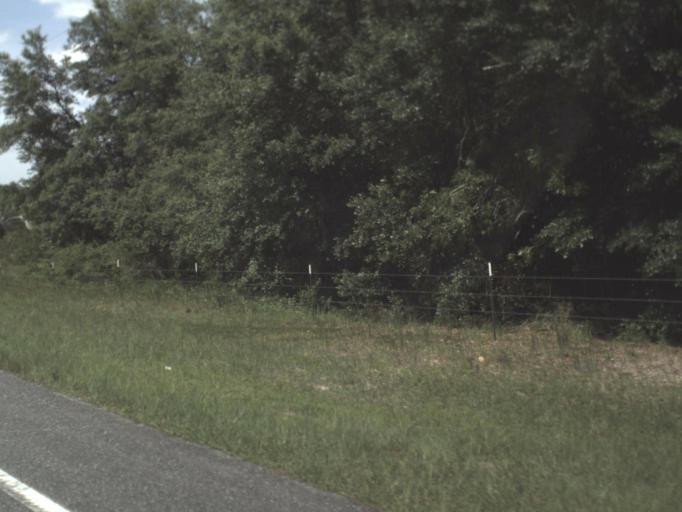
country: US
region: Florida
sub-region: Alachua County
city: High Springs
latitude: 29.7681
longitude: -82.7407
